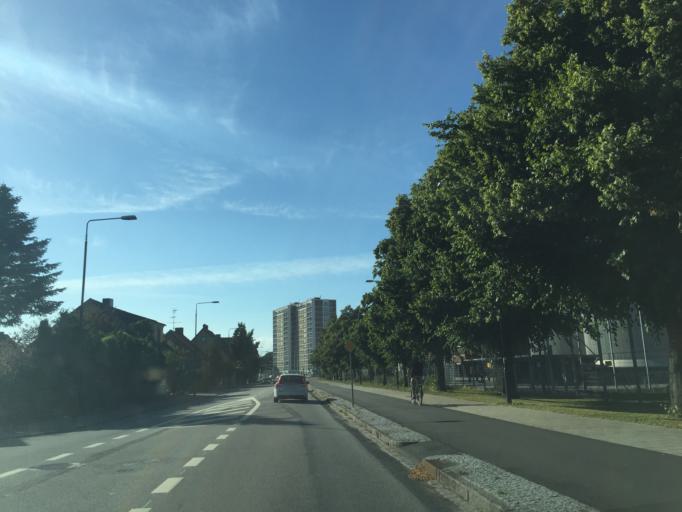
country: SE
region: Skane
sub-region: Malmo
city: Malmoe
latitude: 55.5768
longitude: 13.0130
